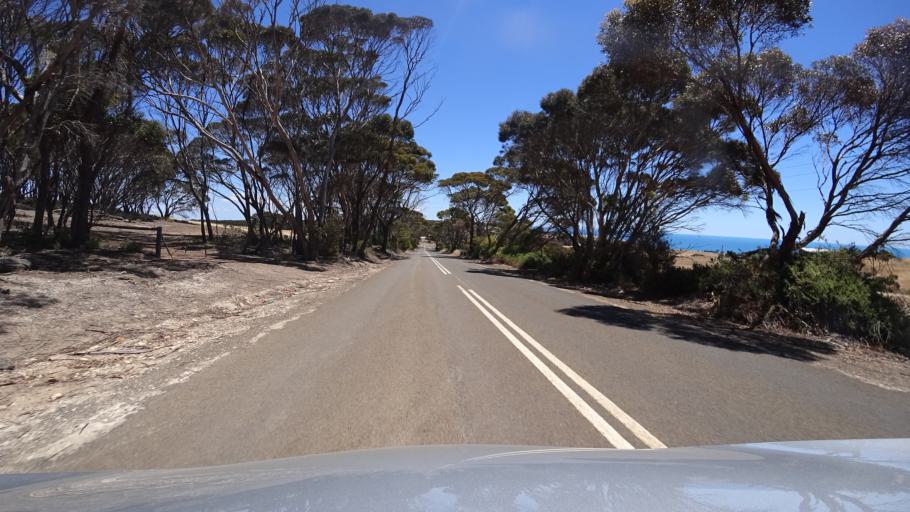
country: AU
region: South Australia
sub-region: Kangaroo Island
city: Kingscote
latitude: -35.7352
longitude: 137.9371
